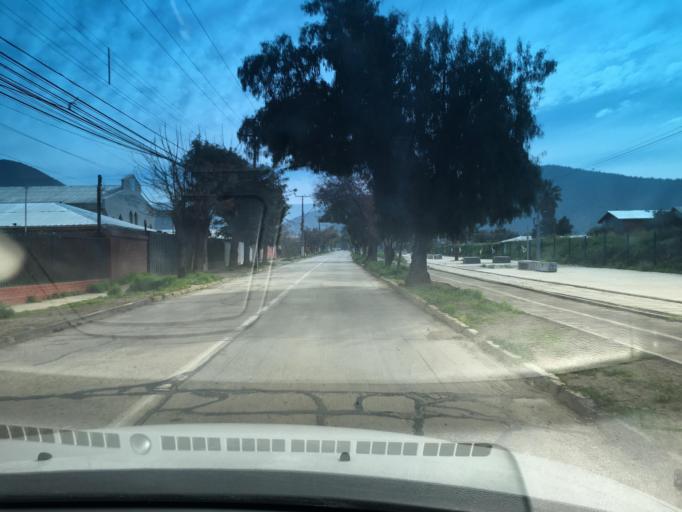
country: CL
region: Santiago Metropolitan
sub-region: Provincia de Chacabuco
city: Lampa
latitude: -33.0807
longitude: -70.9278
